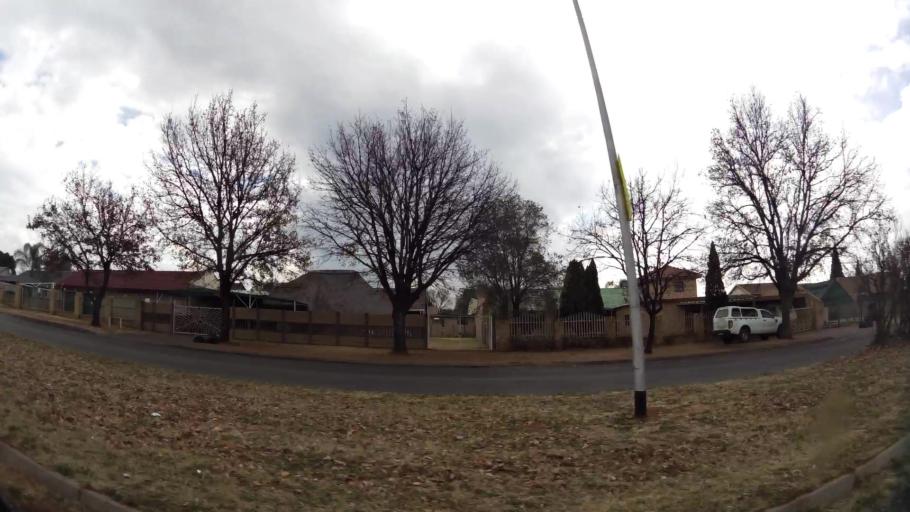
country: ZA
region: Gauteng
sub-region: Sedibeng District Municipality
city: Vanderbijlpark
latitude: -26.7301
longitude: 27.8574
